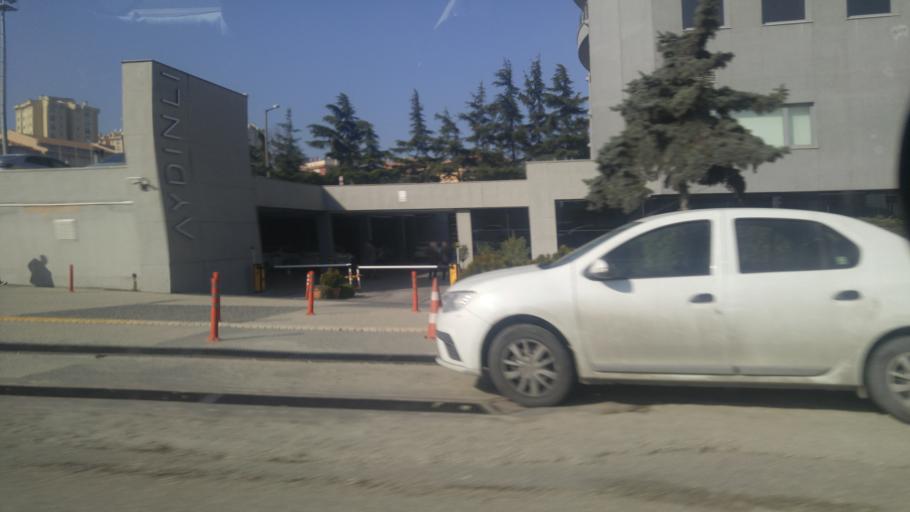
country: TR
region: Istanbul
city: Chekmejeh
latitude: 41.0137
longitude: 28.5430
